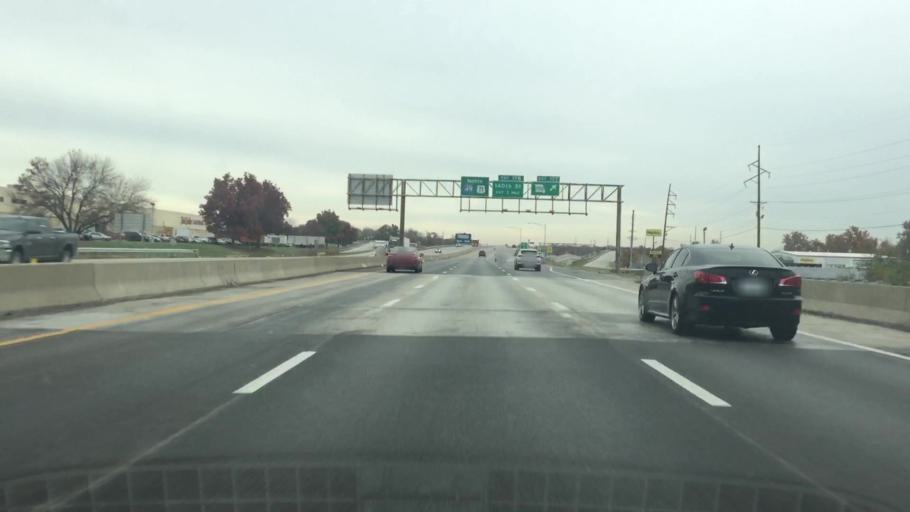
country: US
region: Missouri
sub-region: Jackson County
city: Grandview
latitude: 38.8527
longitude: -94.5287
